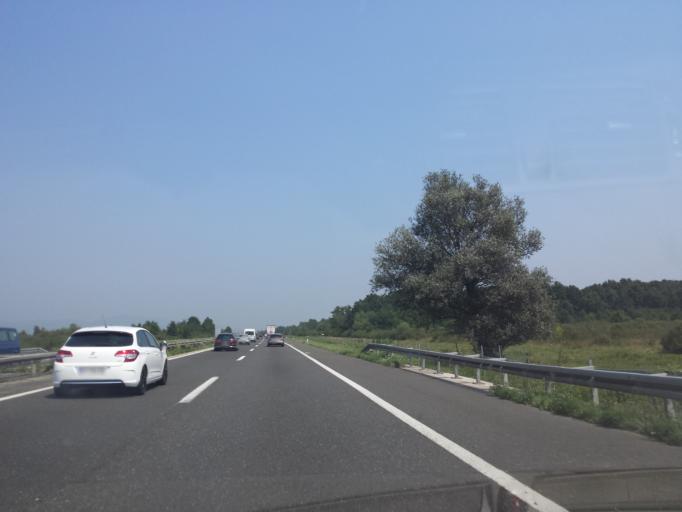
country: HR
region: Zagrebacka
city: Jastrebarsko
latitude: 45.5767
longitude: 15.6217
